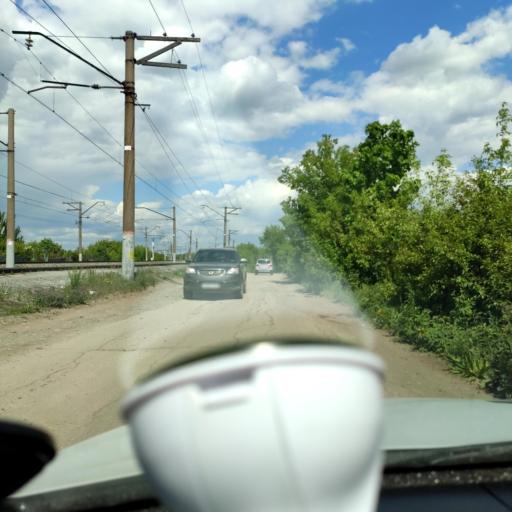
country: RU
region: Samara
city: Petra-Dubrava
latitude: 53.2726
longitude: 50.3180
